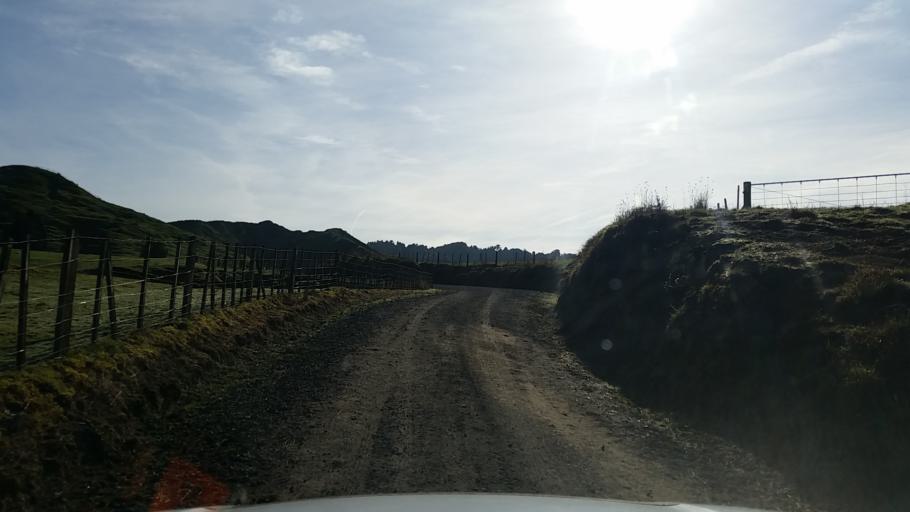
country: NZ
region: Taranaki
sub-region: South Taranaki District
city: Eltham
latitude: -39.3139
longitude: 174.5355
